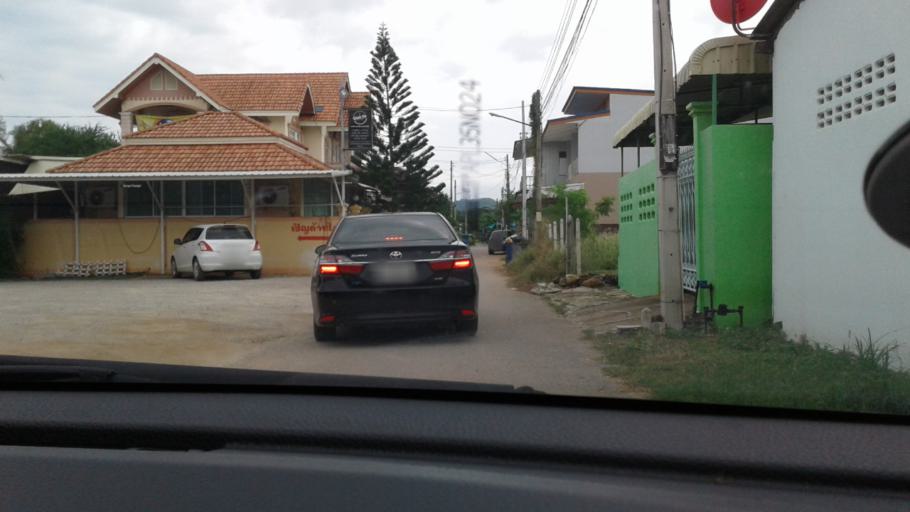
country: TH
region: Prachuap Khiri Khan
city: Pran Buri
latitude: 12.3884
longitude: 99.9877
